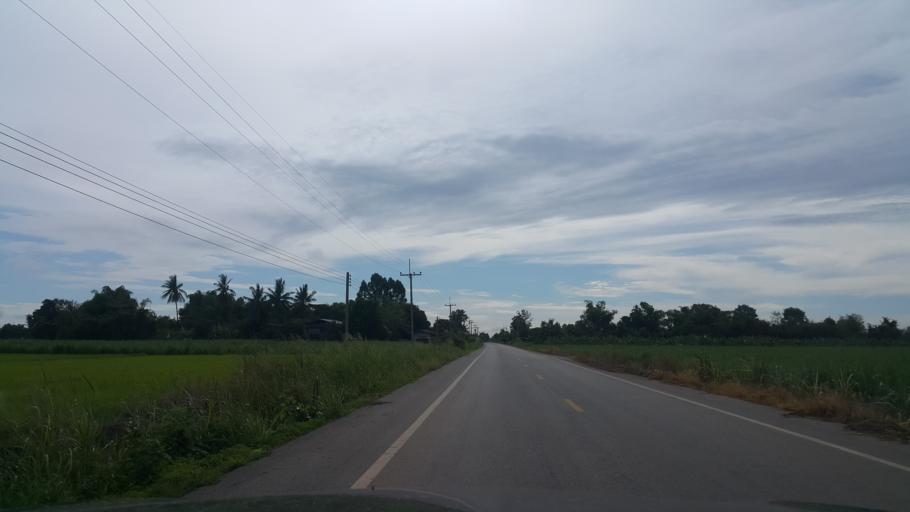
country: TH
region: Sukhothai
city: Si Nakhon
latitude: 17.2618
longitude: 99.9304
